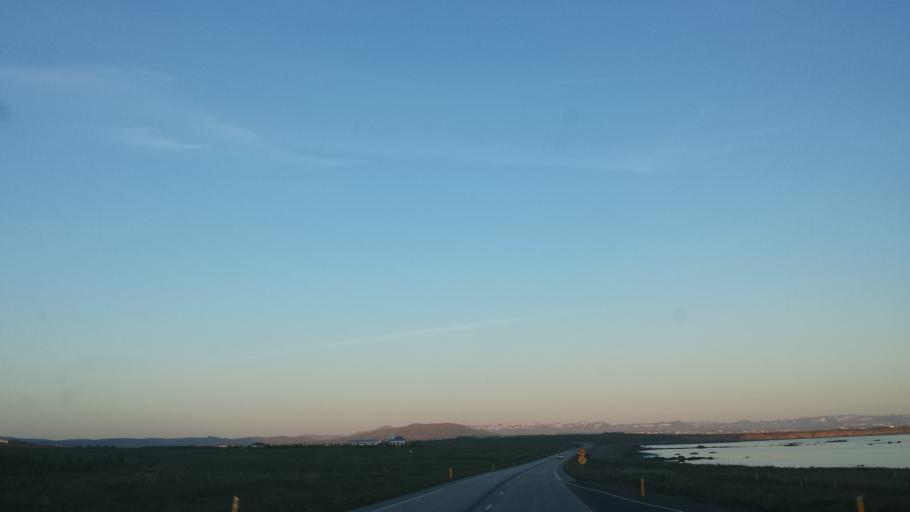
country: IS
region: Capital Region
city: Reykjavik
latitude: 64.2345
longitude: -21.8195
